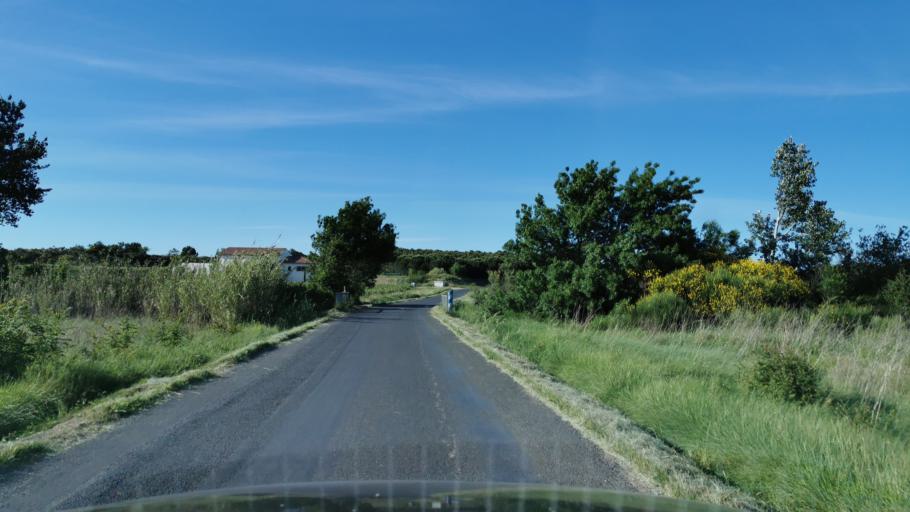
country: FR
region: Languedoc-Roussillon
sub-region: Departement de l'Aude
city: Nevian
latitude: 43.2169
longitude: 2.9126
